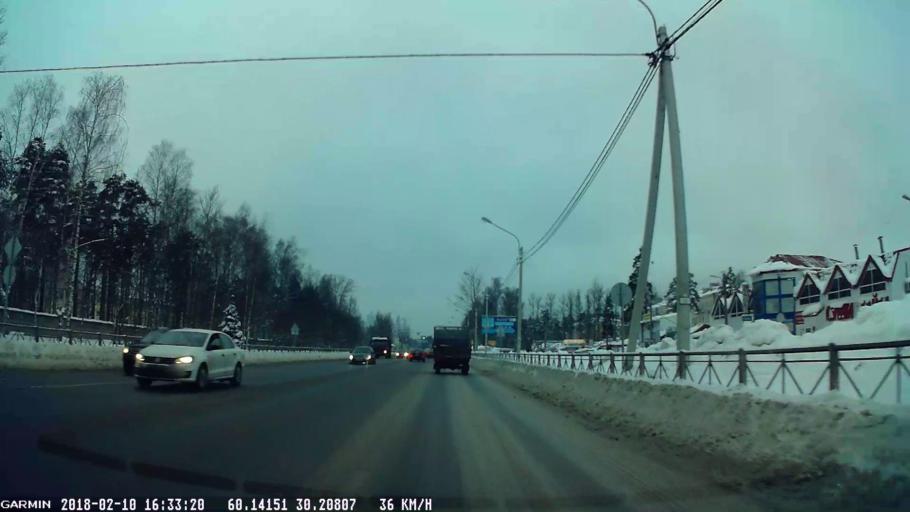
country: RU
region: Leningrad
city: Sertolovo
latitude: 60.1421
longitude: 30.2074
